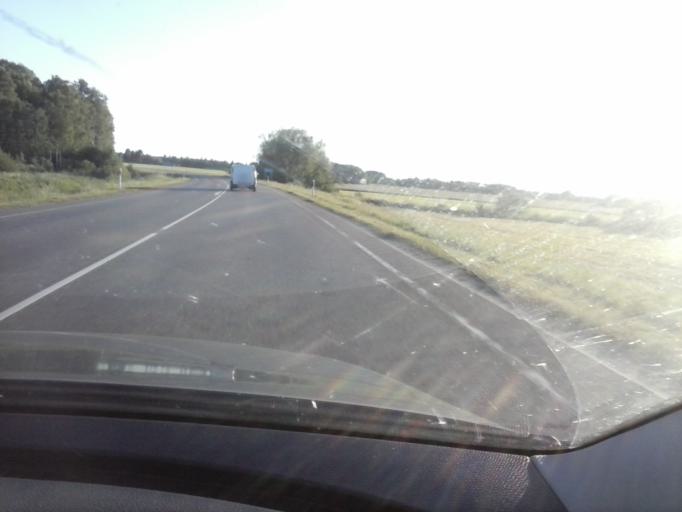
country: EE
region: Laeaene
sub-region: Ridala Parish
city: Uuemoisa
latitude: 58.9737
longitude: 23.8518
